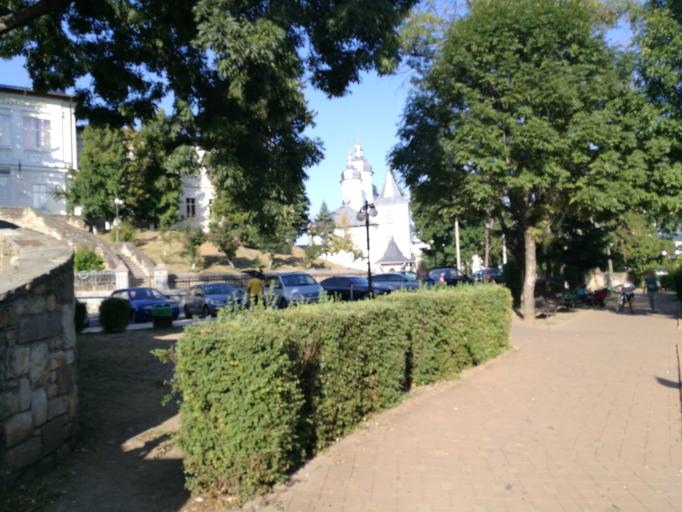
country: RO
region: Neamt
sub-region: Municipiul Piatra-Neamt
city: Valeni
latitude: 46.9326
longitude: 26.3693
